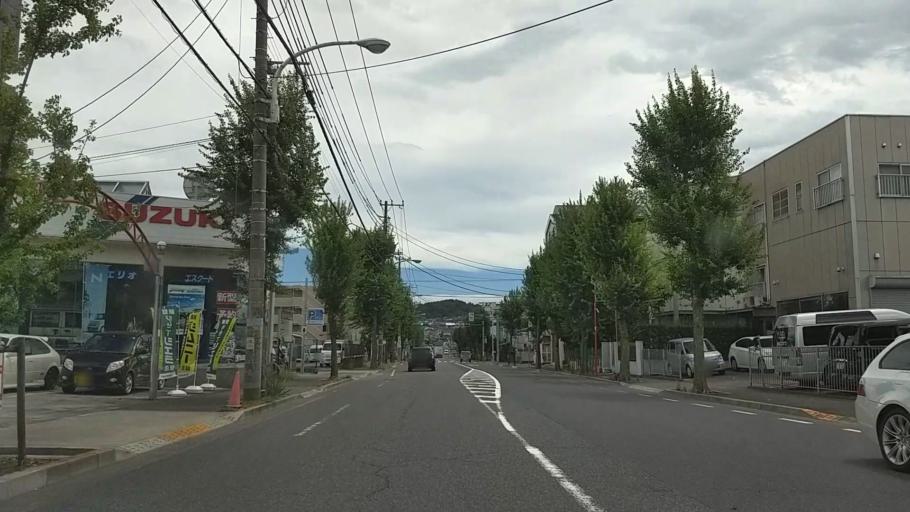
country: JP
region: Tokyo
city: Hachioji
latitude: 35.6478
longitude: 139.3592
